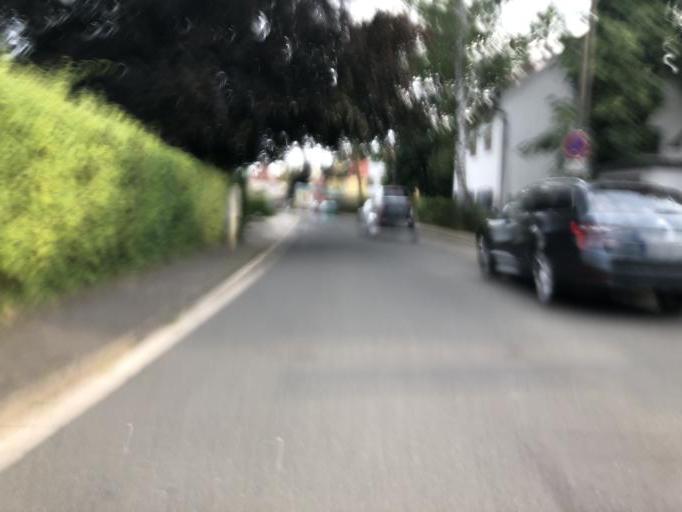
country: DE
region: Bavaria
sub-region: Regierungsbezirk Mittelfranken
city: Erlangen
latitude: 49.5908
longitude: 10.9941
